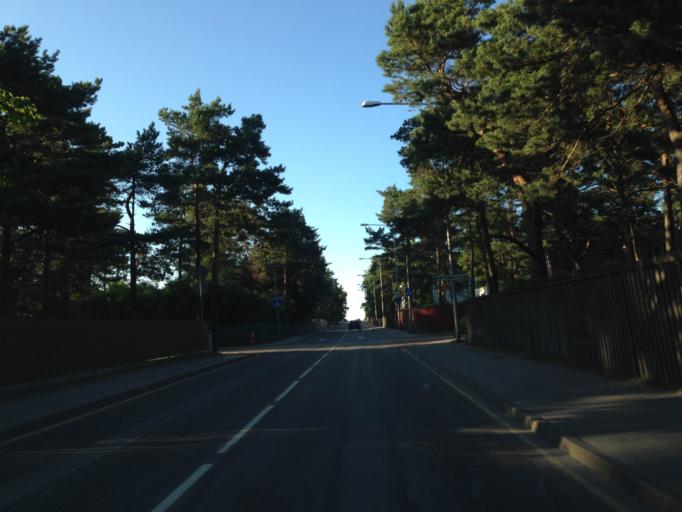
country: EE
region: Harju
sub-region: Saue vald
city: Laagri
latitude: 59.3807
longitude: 24.6374
